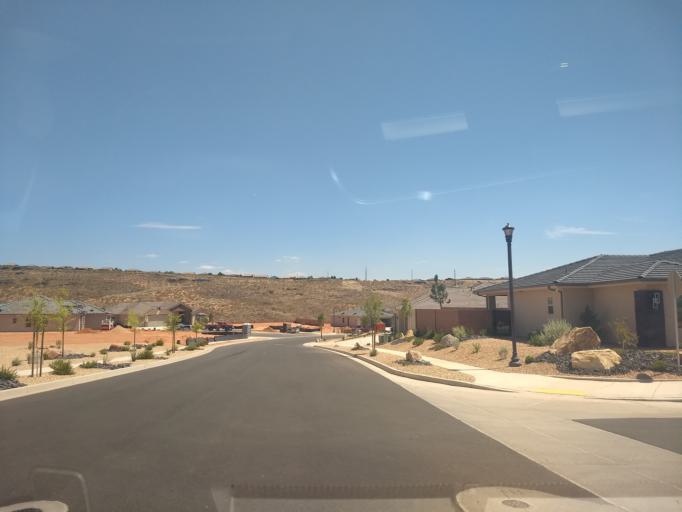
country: US
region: Utah
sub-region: Washington County
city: Washington
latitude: 37.1413
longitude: -113.4788
